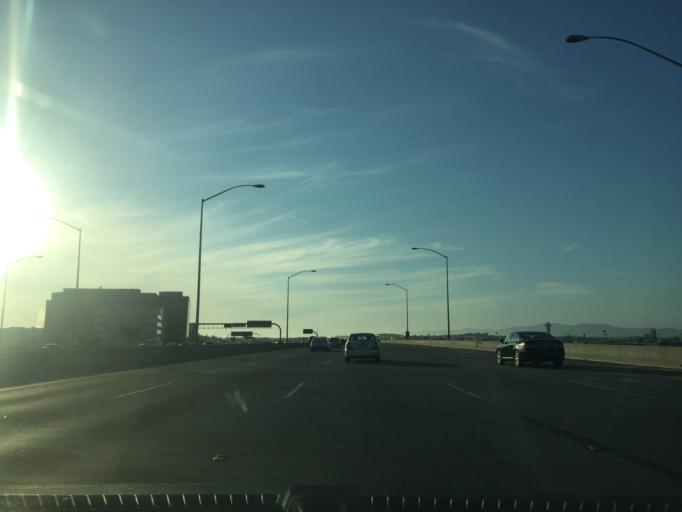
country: US
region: California
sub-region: Los Angeles County
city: Del Aire
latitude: 33.9308
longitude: -118.3783
